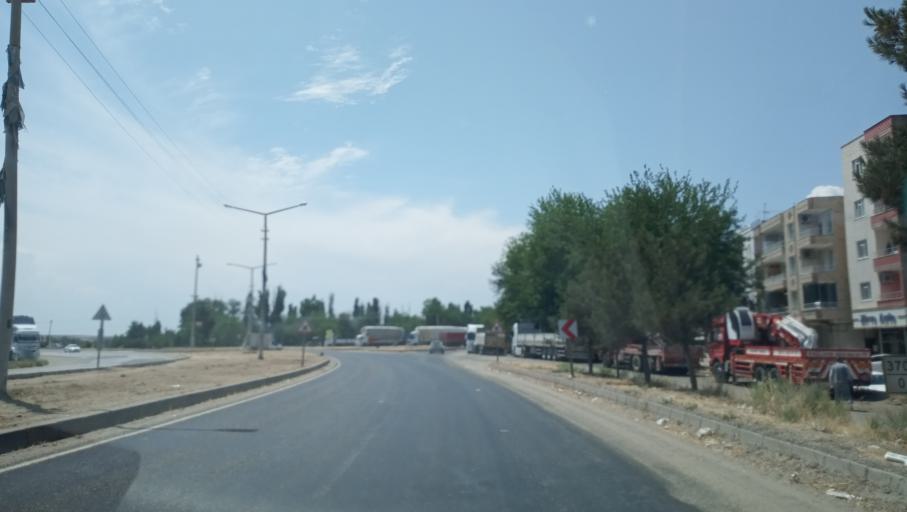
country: TR
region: Diyarbakir
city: Bismil
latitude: 37.8435
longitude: 40.6613
